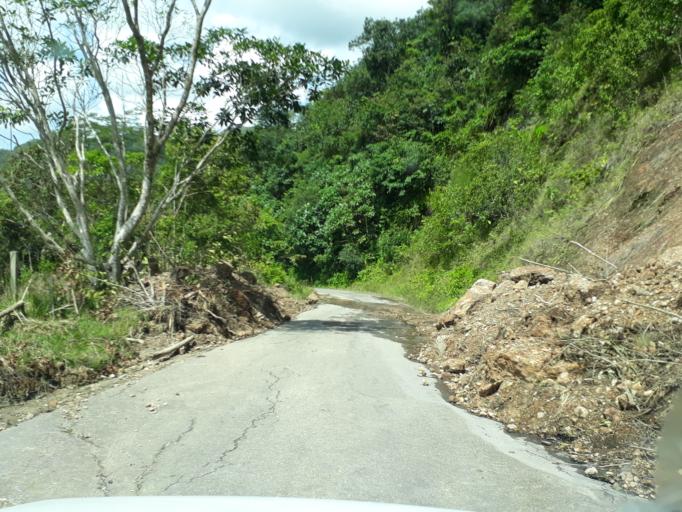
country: CO
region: Cundinamarca
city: Medina
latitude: 4.6352
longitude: -73.3127
